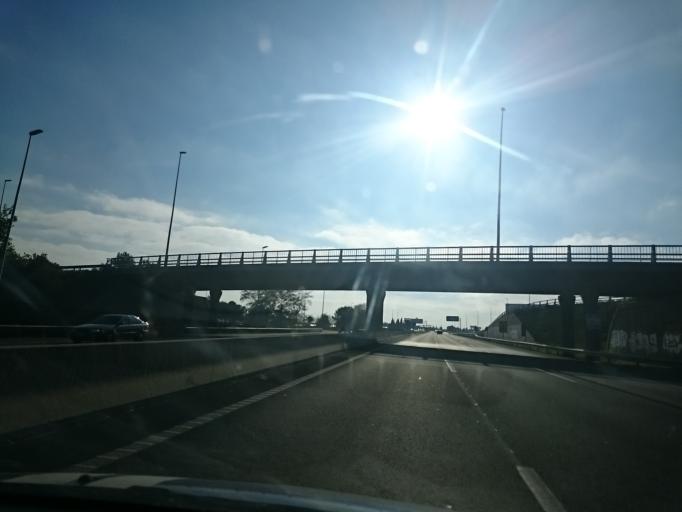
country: ES
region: Catalonia
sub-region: Provincia de Barcelona
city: Viladecans
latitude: 41.3038
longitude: 2.0251
